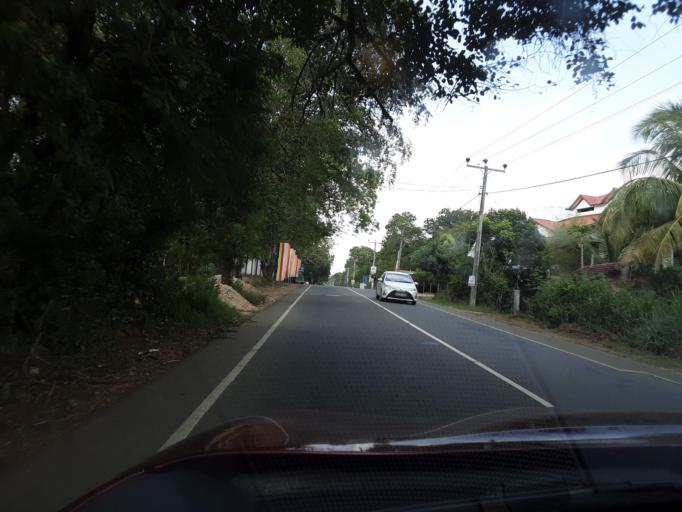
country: LK
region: Uva
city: Haputale
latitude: 6.5276
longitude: 81.1254
